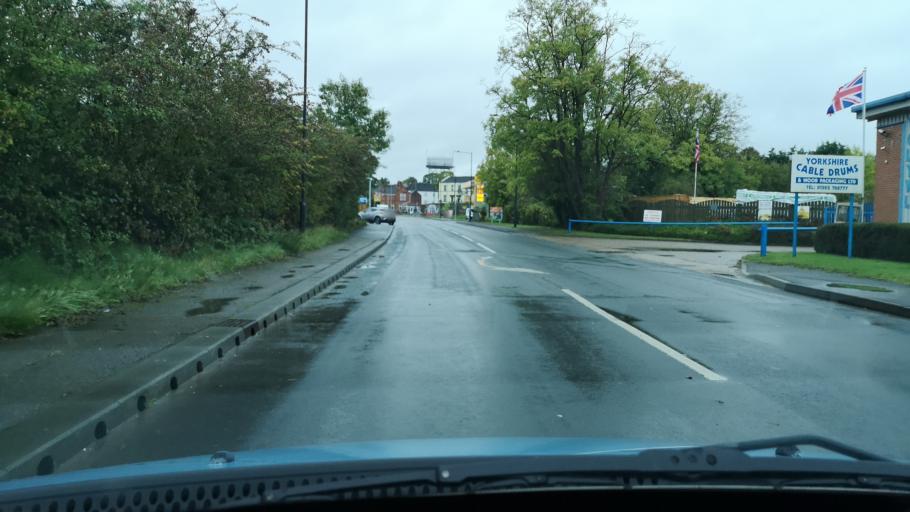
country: GB
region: England
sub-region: Doncaster
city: Askern
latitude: 53.6203
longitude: -1.1535
